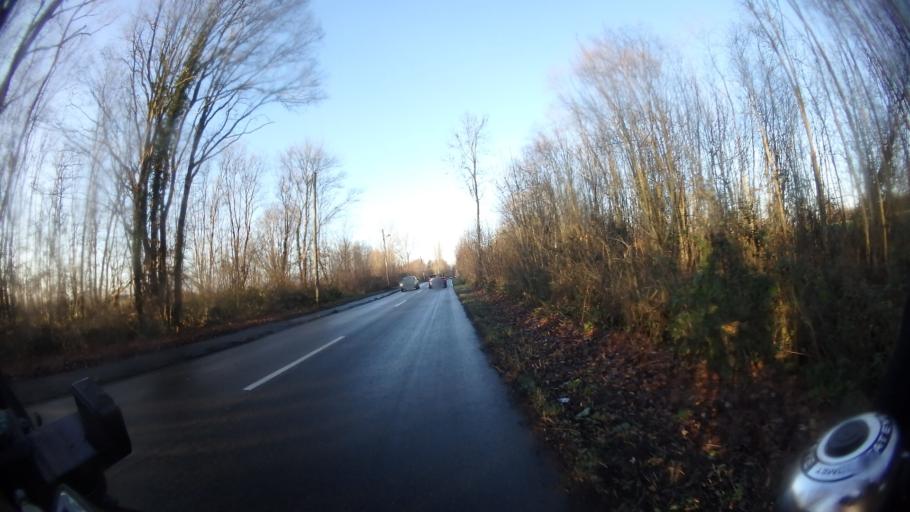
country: DE
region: Schleswig-Holstein
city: Travemuende
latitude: 53.9810
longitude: 10.8641
